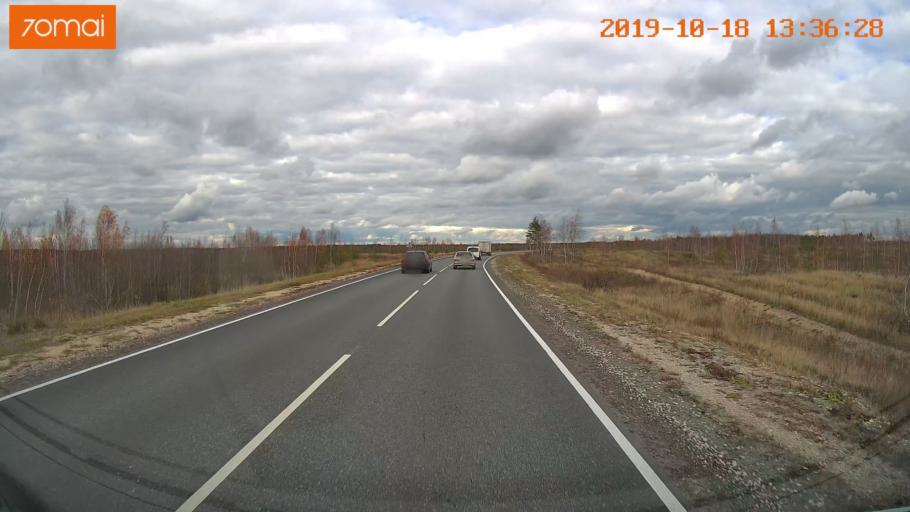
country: RU
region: Rjazan
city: Solotcha
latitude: 54.8702
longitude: 39.9848
